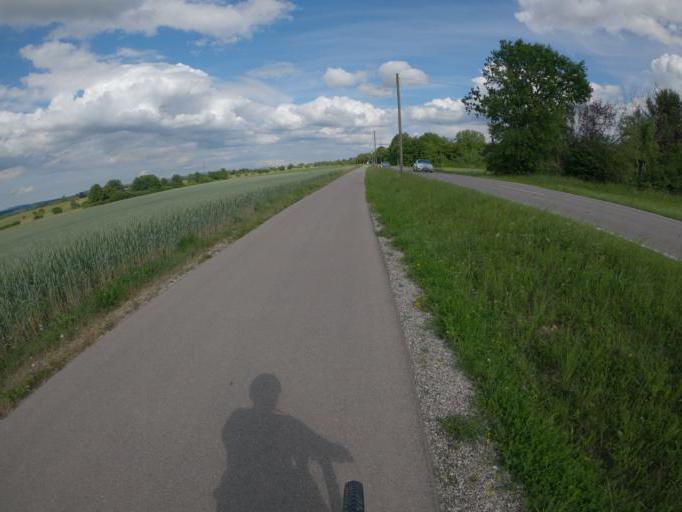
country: DE
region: Baden-Wuerttemberg
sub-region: Regierungsbezirk Stuttgart
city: Hattenhofen
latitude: 48.6653
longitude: 9.5505
